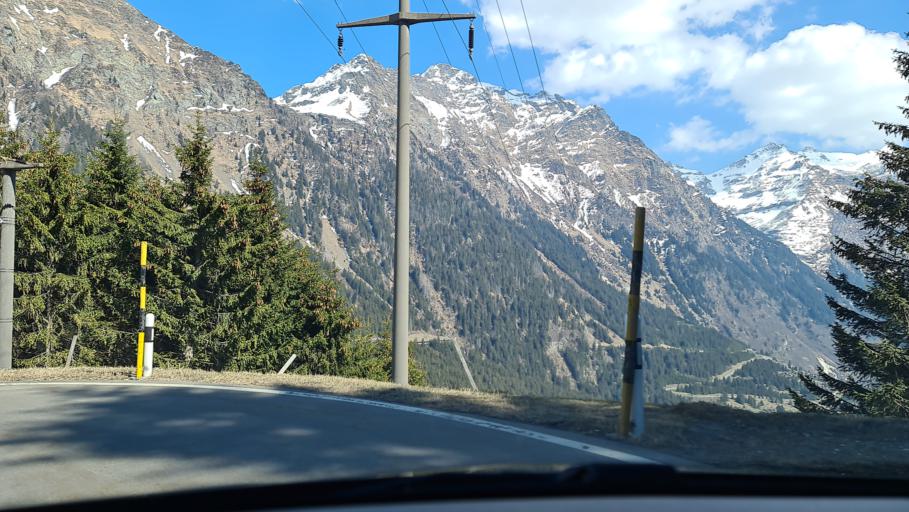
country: CH
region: Grisons
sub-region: Moesa District
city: Mesocco
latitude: 46.4345
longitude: 9.2056
